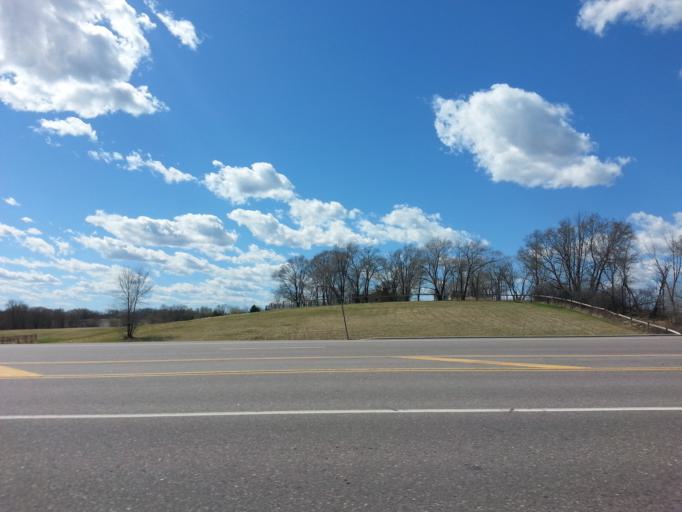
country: US
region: Minnesota
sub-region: Scott County
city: Prior Lake
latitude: 44.7168
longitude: -93.3791
